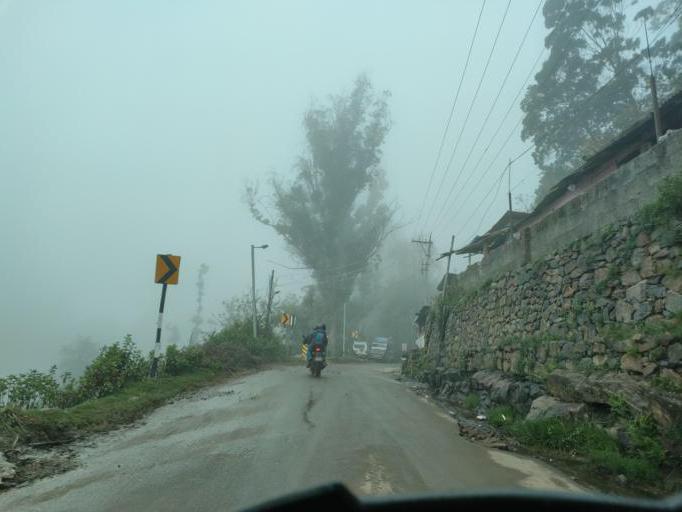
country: IN
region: Tamil Nadu
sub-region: Dindigul
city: Kodaikanal
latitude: 10.2336
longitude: 77.4759
